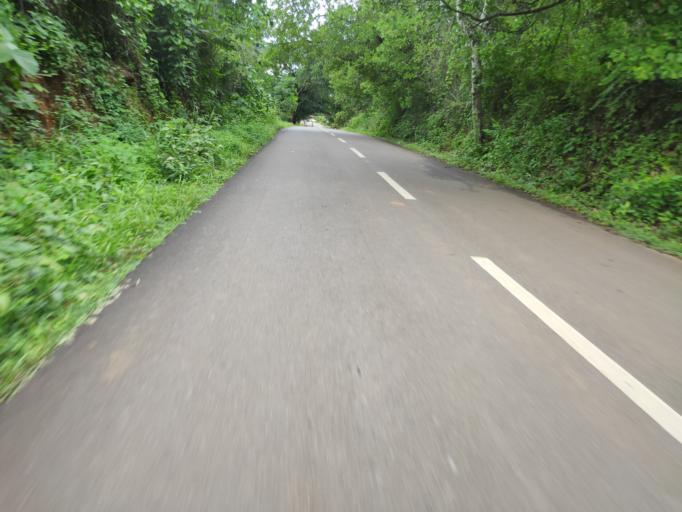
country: IN
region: Kerala
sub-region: Malappuram
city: Manjeri
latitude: 11.1710
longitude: 76.1825
